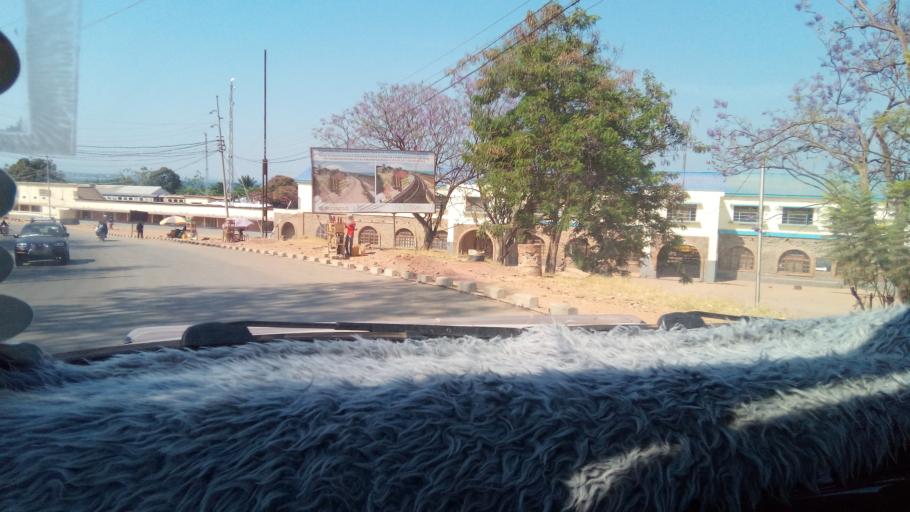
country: CD
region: Katanga
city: Kalemie
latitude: -5.9468
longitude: 29.1971
